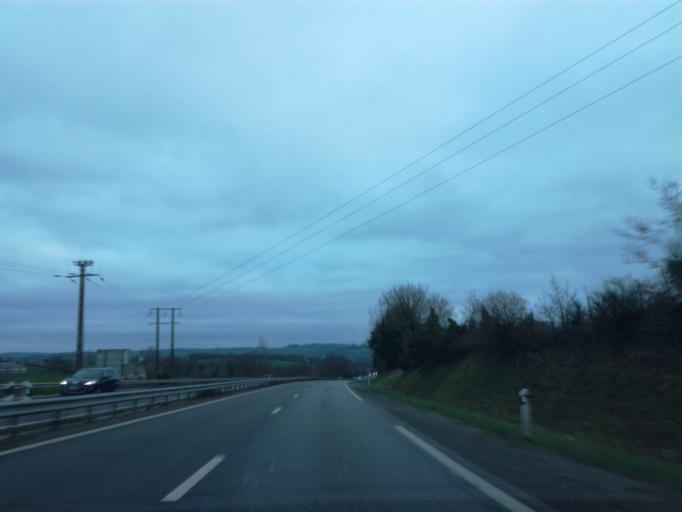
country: FR
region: Brittany
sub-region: Departement des Cotes-d'Armor
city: Saint-Barnabe
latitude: 48.1788
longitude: -2.6622
